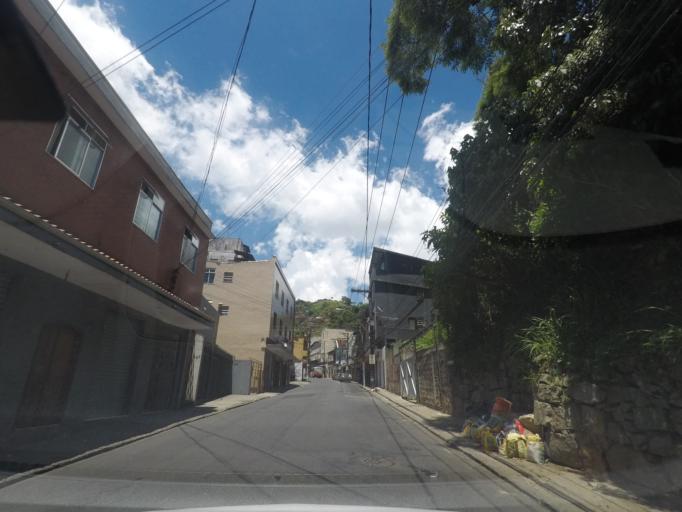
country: BR
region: Rio de Janeiro
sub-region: Petropolis
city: Petropolis
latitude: -22.5139
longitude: -43.1742
